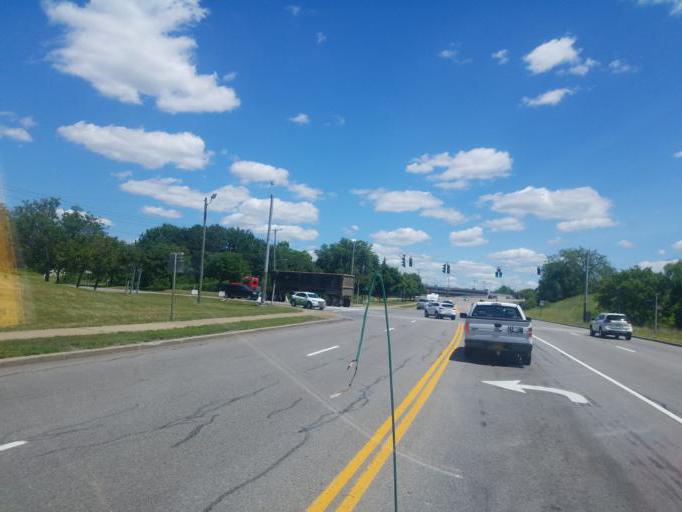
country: US
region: New York
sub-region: Erie County
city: Blasdell
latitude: 42.7893
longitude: -78.8208
